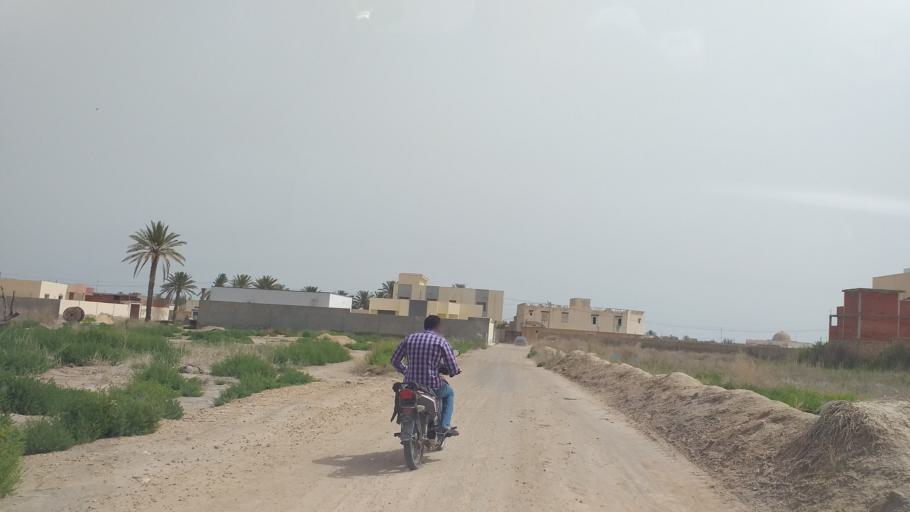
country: TN
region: Qabis
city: Gabes
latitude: 33.9426
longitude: 10.0559
